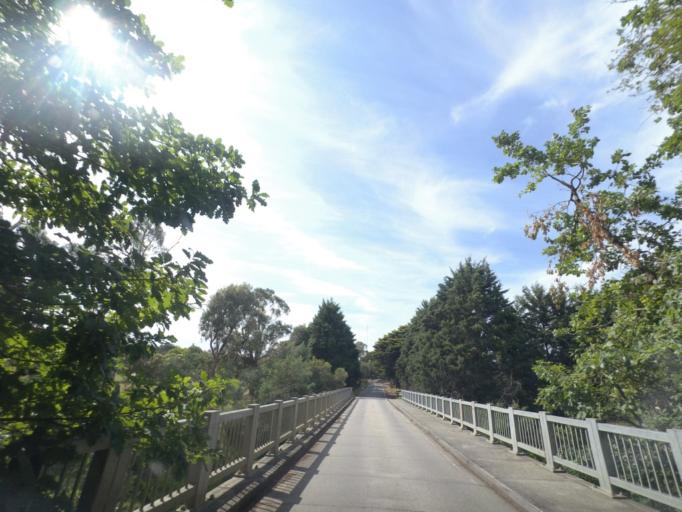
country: AU
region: Victoria
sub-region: Banyule
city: Viewbank
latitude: -37.7393
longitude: 145.1050
